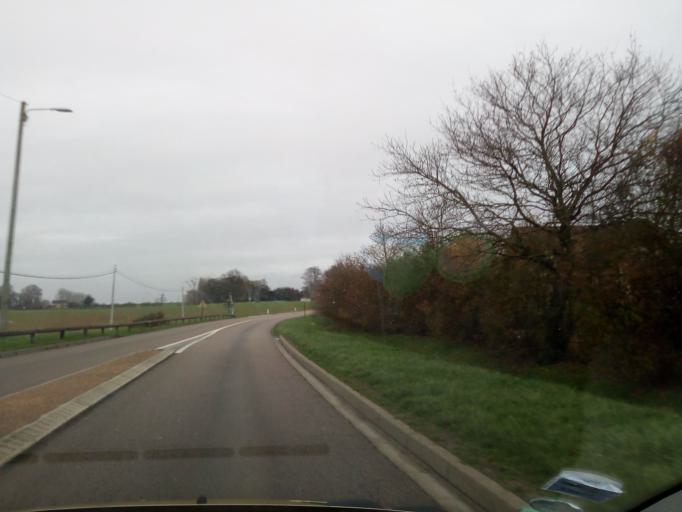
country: FR
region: Haute-Normandie
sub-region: Departement de l'Eure
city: Hauville
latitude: 49.3847
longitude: 0.7993
